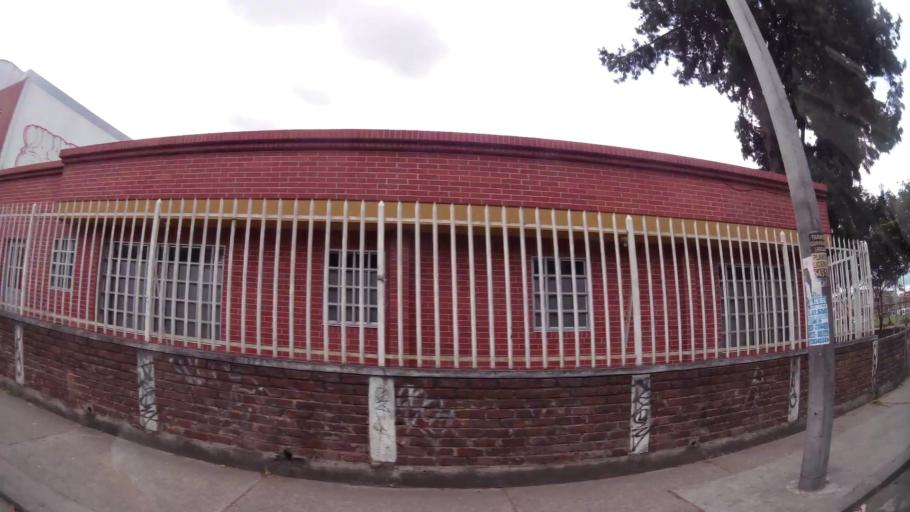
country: CO
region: Cundinamarca
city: Funza
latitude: 4.7105
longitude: -74.1199
